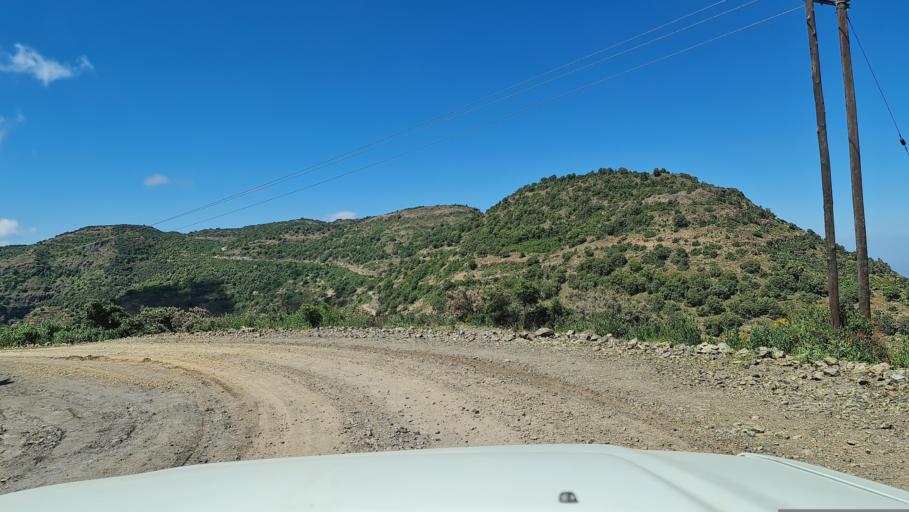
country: ET
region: Amhara
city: Debark'
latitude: 13.2331
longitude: 38.0672
